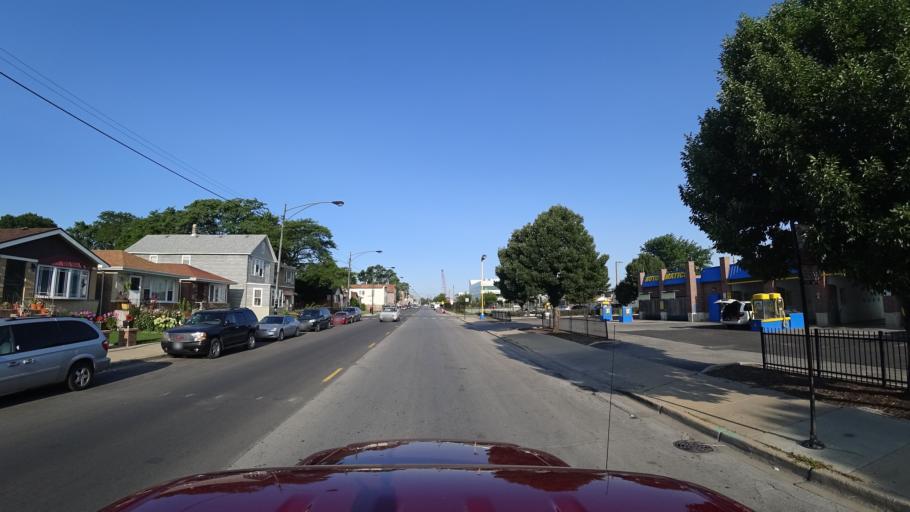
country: US
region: Illinois
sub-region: Cook County
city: Cicero
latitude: 41.8008
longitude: -87.7067
